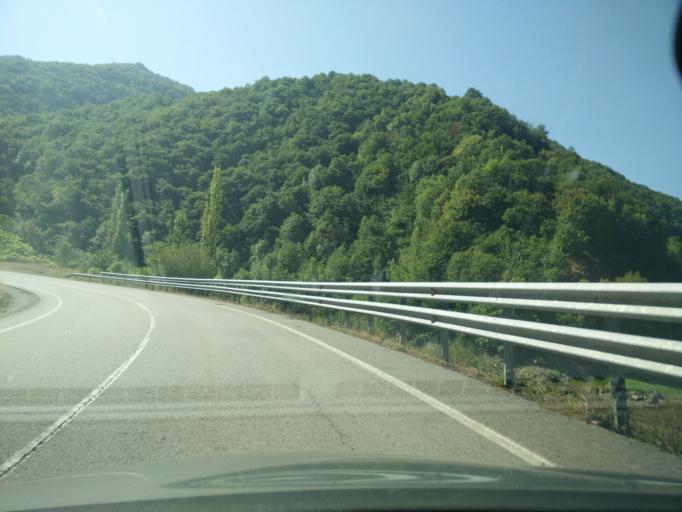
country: ES
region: Asturias
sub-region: Province of Asturias
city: Campo de Caso
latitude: 43.1910
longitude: -5.3815
